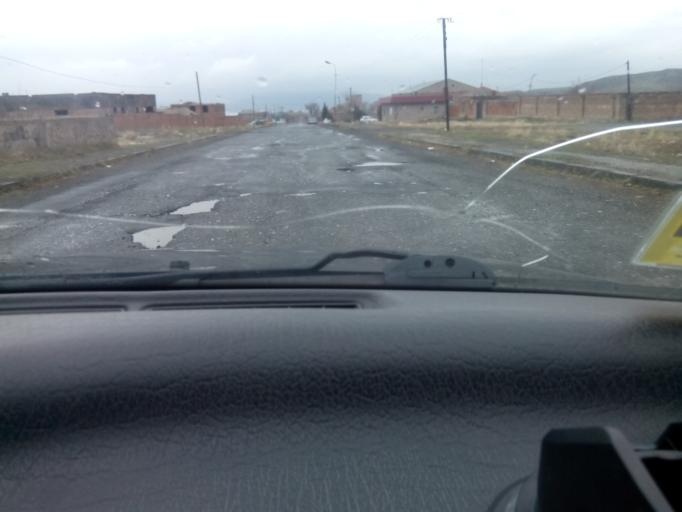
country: AM
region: Aragatsotn
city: T'alin
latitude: 40.3866
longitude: 43.8959
